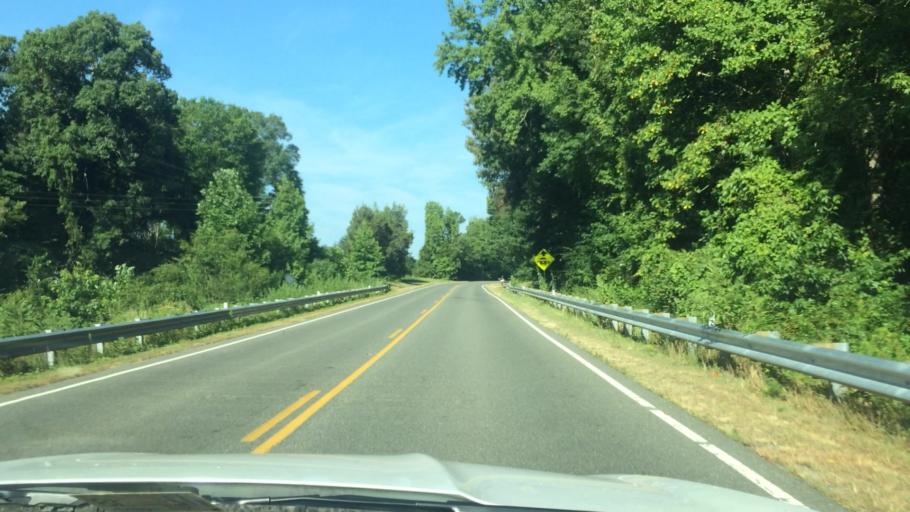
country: US
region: Virginia
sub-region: Northumberland County
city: Heathsville
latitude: 37.8498
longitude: -76.5957
